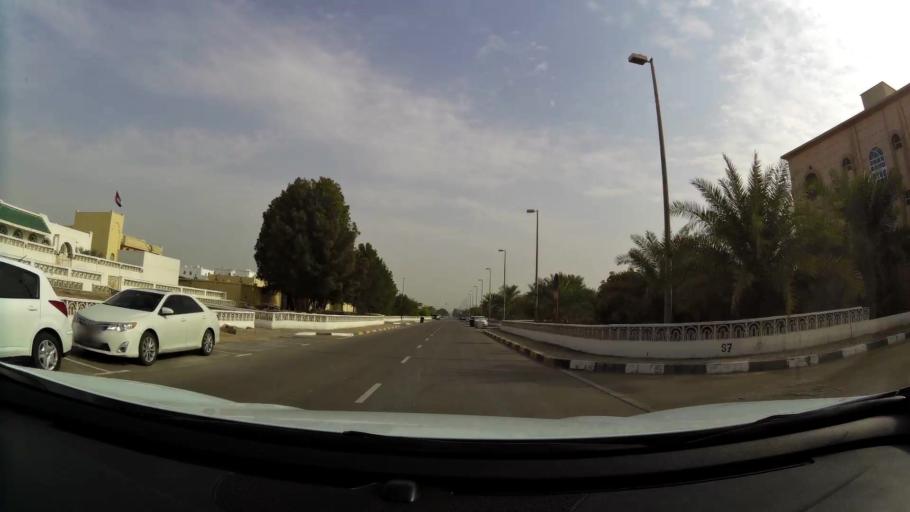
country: AE
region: Abu Dhabi
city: Abu Dhabi
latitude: 24.6683
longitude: 54.7521
